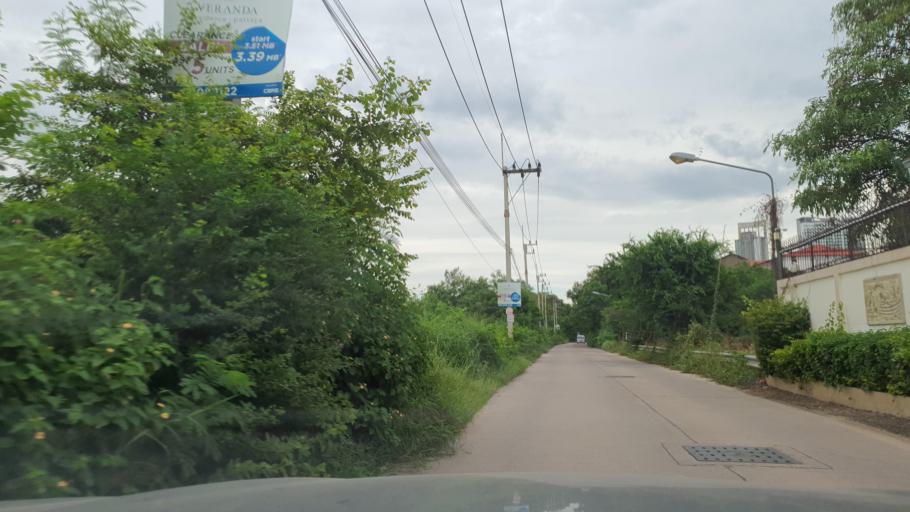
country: TH
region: Chon Buri
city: Phatthaya
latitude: 12.8677
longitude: 100.8979
